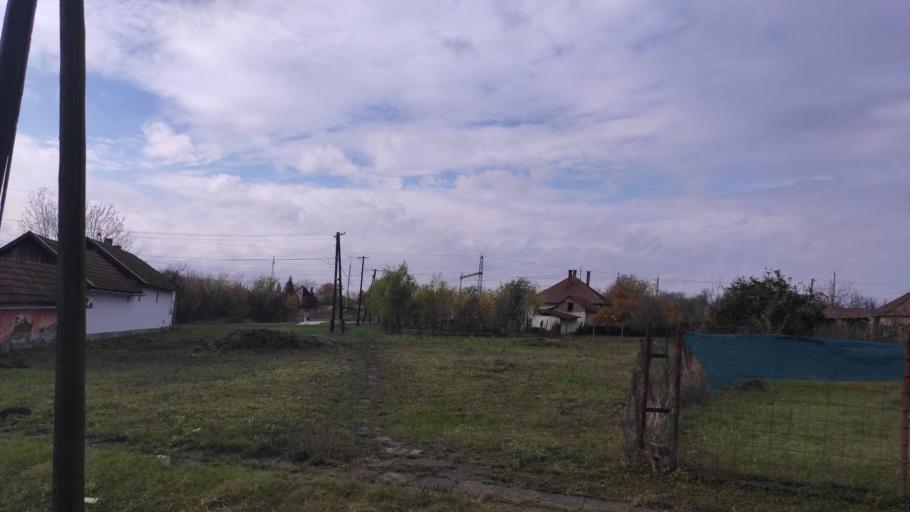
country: HU
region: Bekes
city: Mezobereny
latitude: 46.7607
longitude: 21.0385
